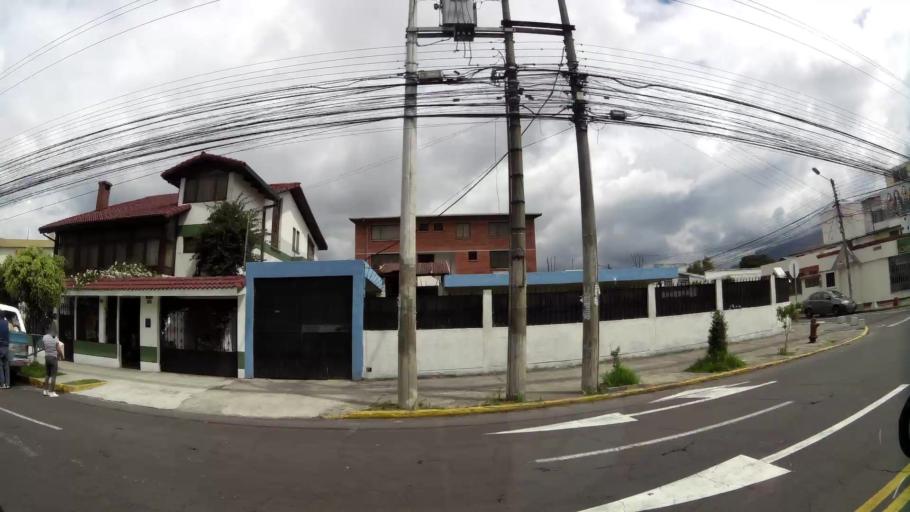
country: EC
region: Pichincha
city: Quito
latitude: -0.1625
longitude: -78.4803
